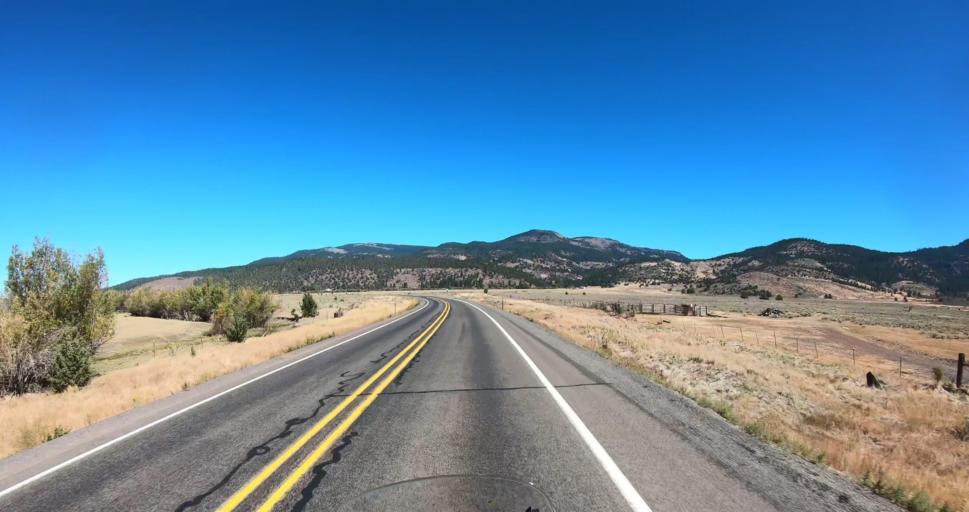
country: US
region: Oregon
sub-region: Lake County
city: Lakeview
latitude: 42.3279
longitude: -120.3030
